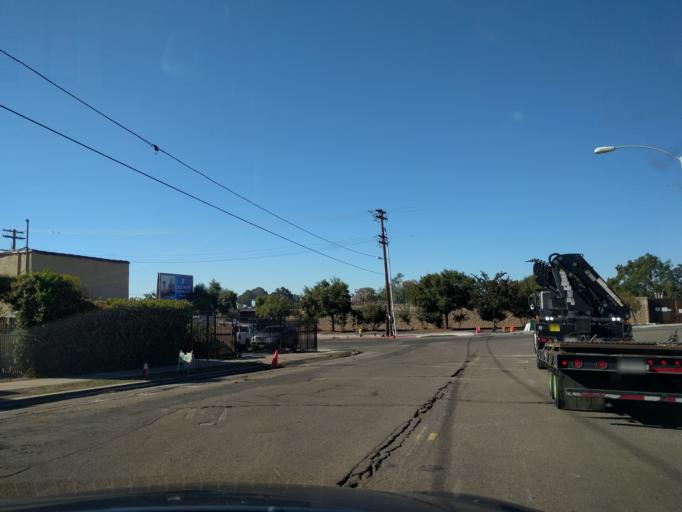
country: US
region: California
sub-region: San Diego County
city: San Diego
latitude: 32.7128
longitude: -117.1297
